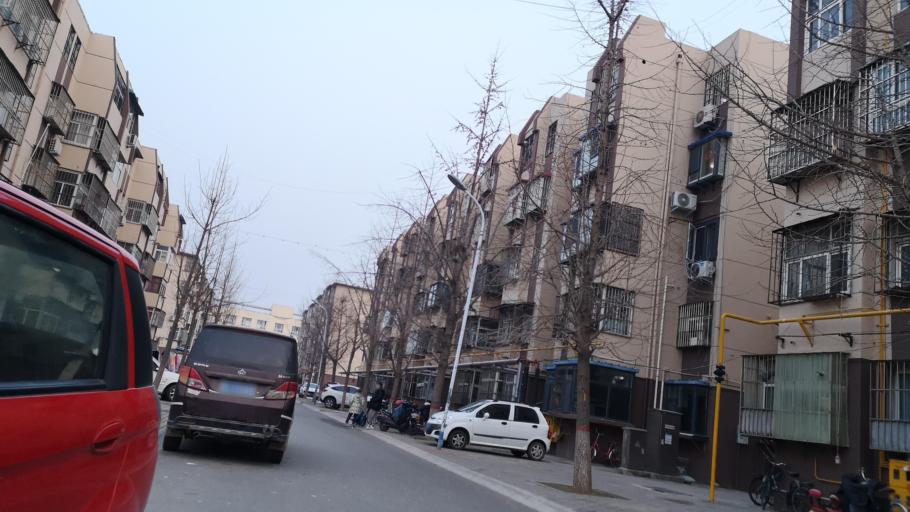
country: CN
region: Henan Sheng
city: Zhongyuanlu
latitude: 35.7831
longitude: 115.0734
